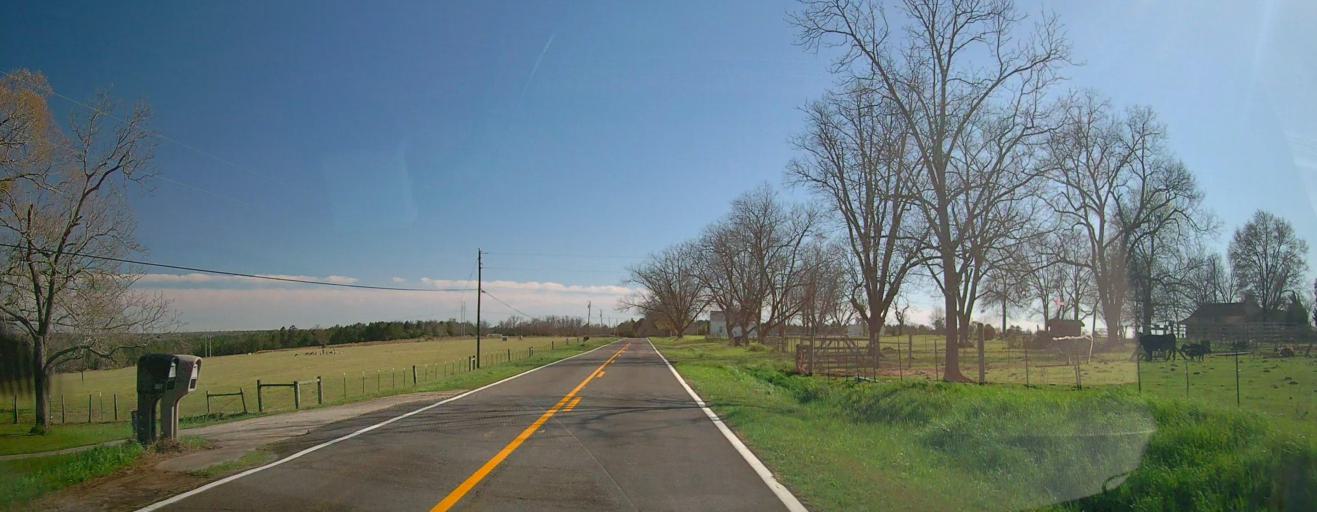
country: US
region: Georgia
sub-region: Peach County
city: Fort Valley
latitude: 32.6328
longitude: -83.8988
